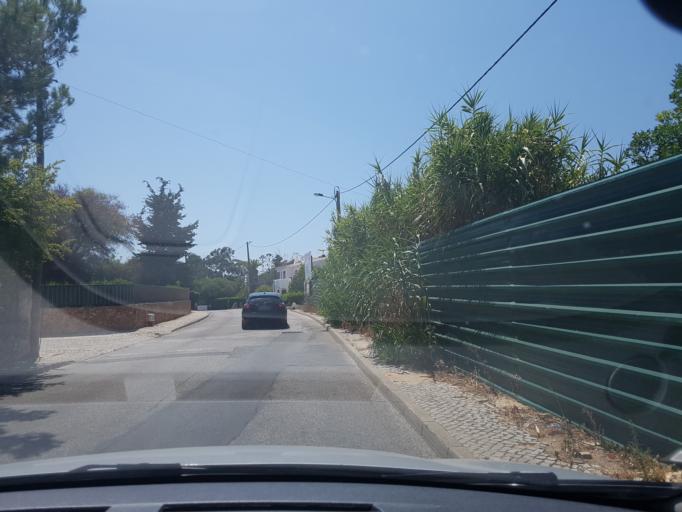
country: PT
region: Faro
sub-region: Lagoa
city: Carvoeiro
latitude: 37.0974
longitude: -8.4598
